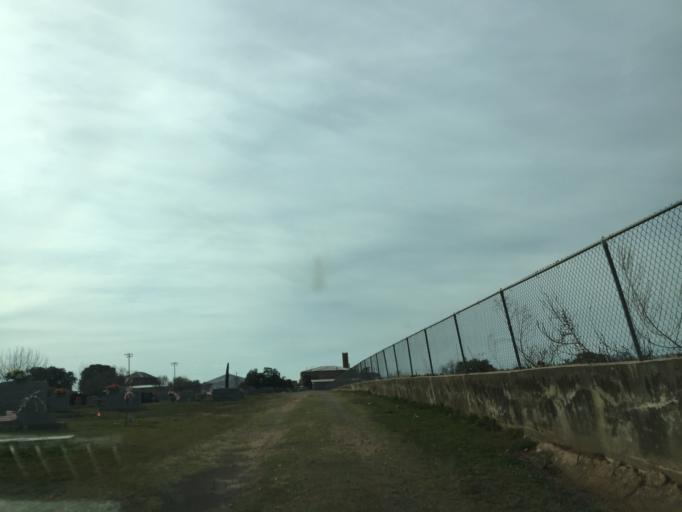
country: US
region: Texas
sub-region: Llano County
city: Llano
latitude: 30.7436
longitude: -98.6703
